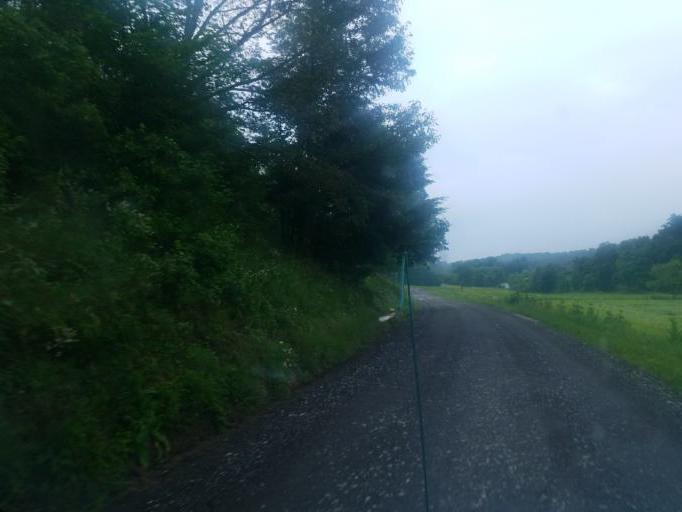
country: US
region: Ohio
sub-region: Columbiana County
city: Salineville
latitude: 40.5786
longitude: -80.9316
